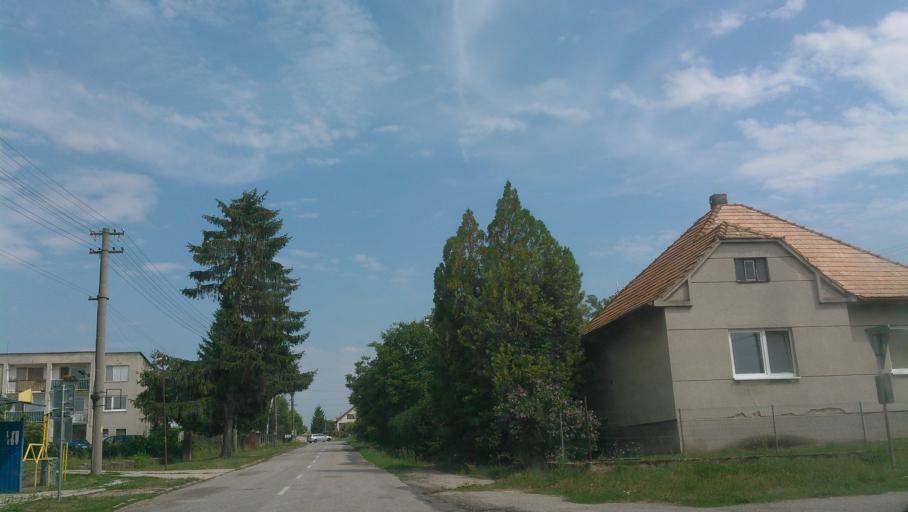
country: SK
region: Nitriansky
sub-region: Okres Nitra
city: Nitra
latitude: 48.5018
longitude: 18.0131
